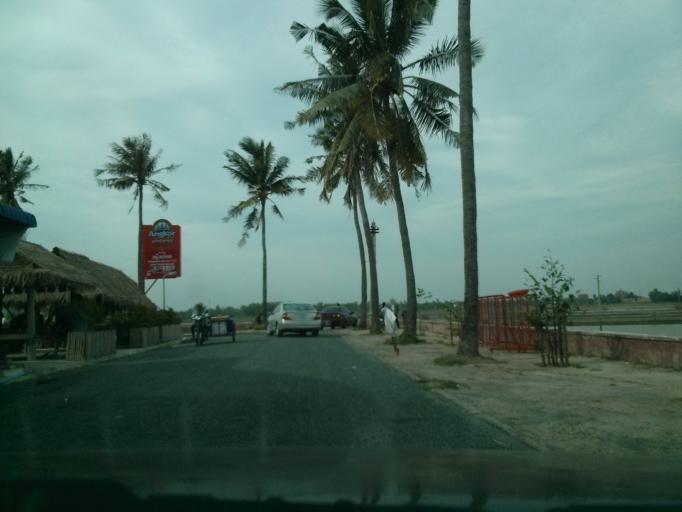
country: KH
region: Takeo
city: Takeo
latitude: 10.9946
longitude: 104.7859
